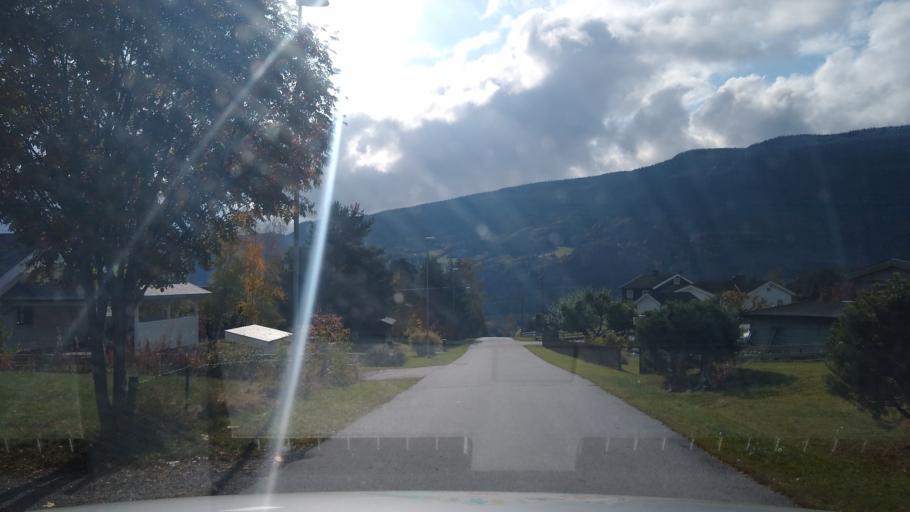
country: NO
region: Oppland
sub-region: Ringebu
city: Ringebu
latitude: 61.5358
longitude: 10.1401
